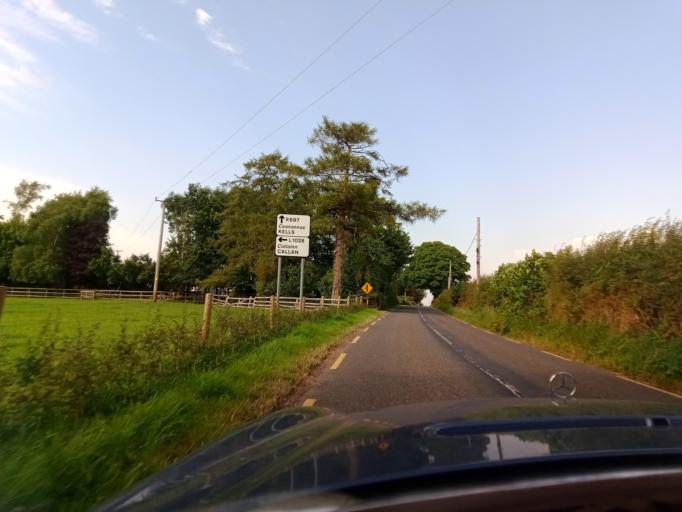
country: IE
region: Leinster
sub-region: Kilkenny
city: Callan
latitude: 52.5135
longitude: -7.3125
